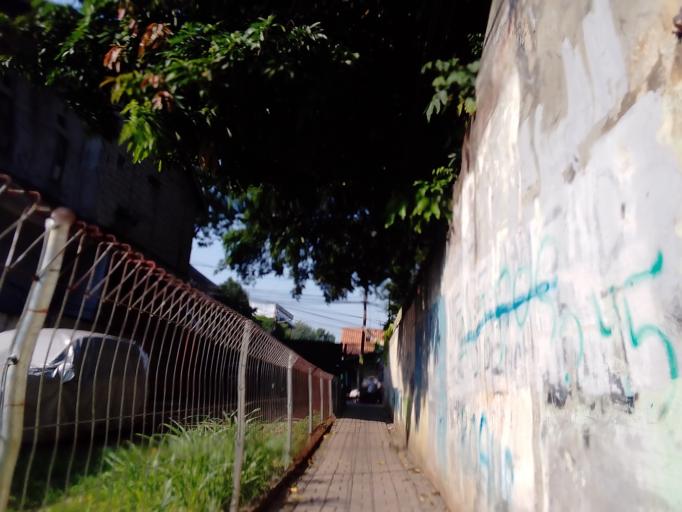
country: ID
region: Jakarta Raya
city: Jakarta
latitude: -6.2656
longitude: 106.8101
